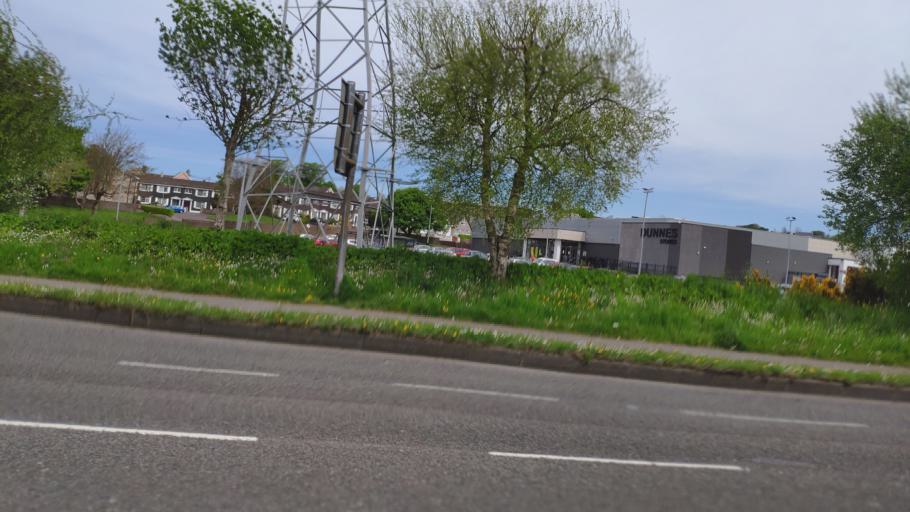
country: IE
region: Munster
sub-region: County Cork
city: Cork
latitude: 51.9153
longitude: -8.4500
